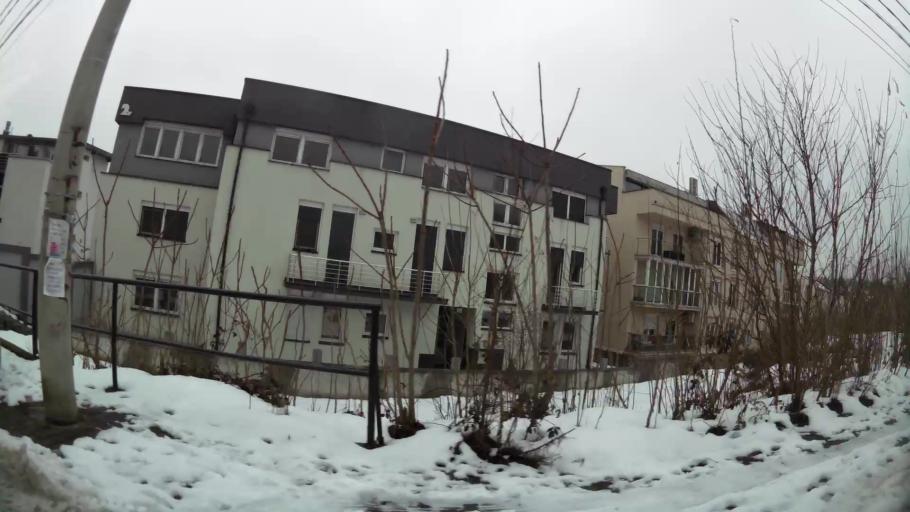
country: RS
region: Central Serbia
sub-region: Belgrade
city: Savski Venac
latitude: 44.7667
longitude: 20.4588
